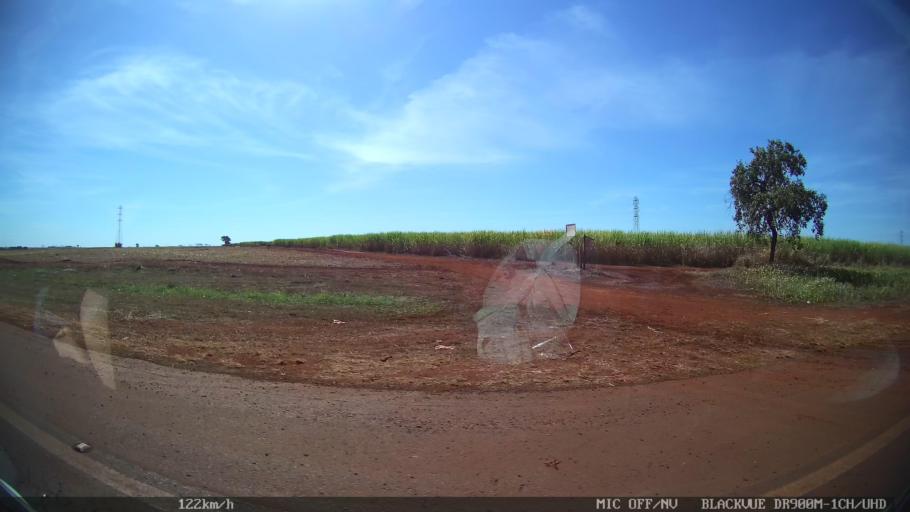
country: BR
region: Sao Paulo
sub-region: Ipua
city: Ipua
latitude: -20.4642
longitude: -48.1314
